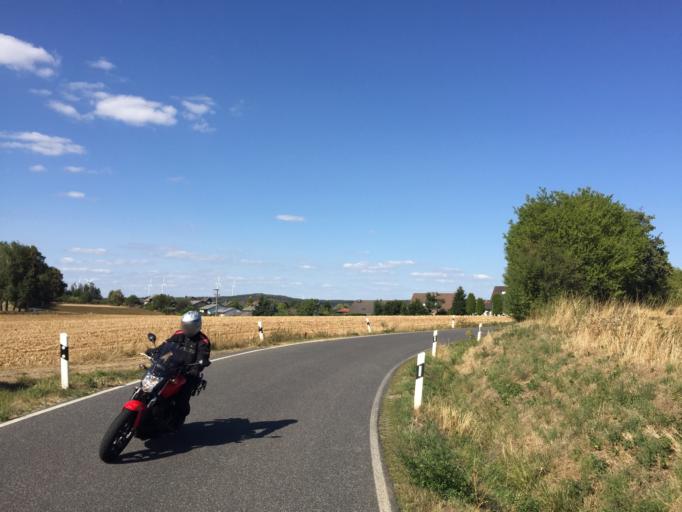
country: DE
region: Hesse
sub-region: Regierungsbezirk Giessen
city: Grunberg
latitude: 50.6146
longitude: 8.9318
